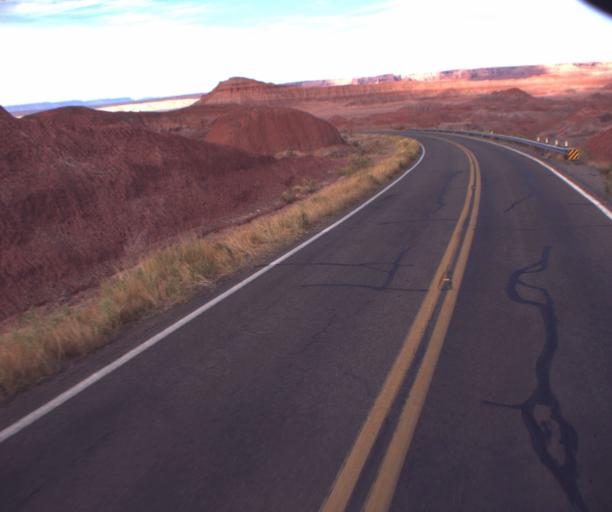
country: US
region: Arizona
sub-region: Apache County
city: Many Farms
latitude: 36.4709
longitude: -109.5584
